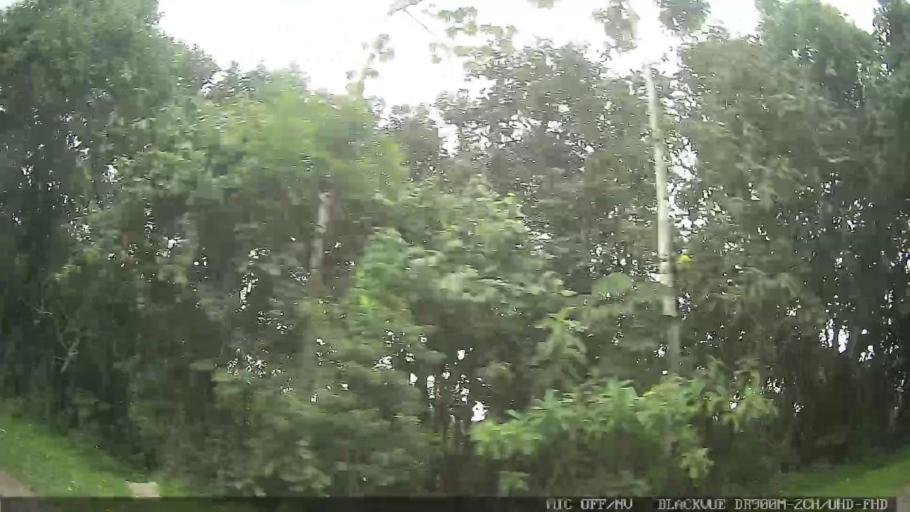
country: BR
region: Sao Paulo
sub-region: Biritiba-Mirim
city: Biritiba Mirim
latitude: -23.5541
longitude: -45.9796
